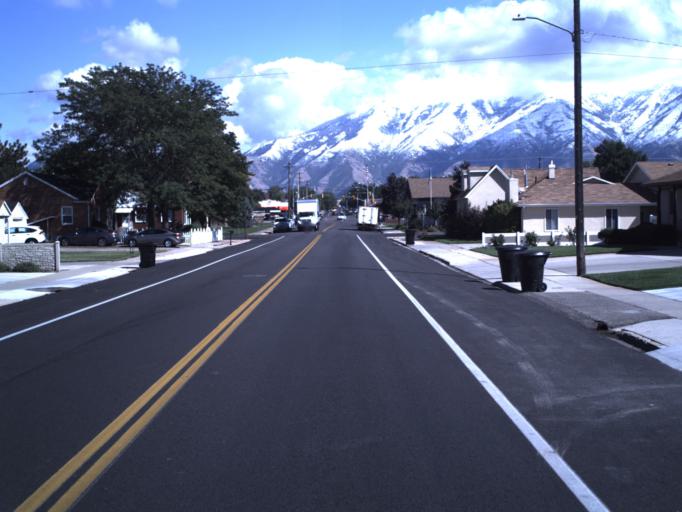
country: US
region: Utah
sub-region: Utah County
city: Spanish Fork
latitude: 40.1150
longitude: -111.6577
